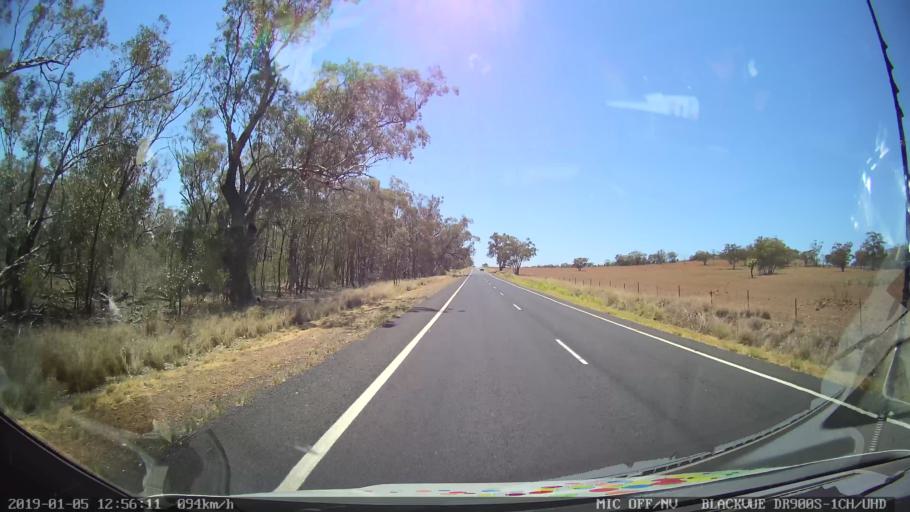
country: AU
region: New South Wales
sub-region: Warrumbungle Shire
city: Coonabarabran
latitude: -31.1162
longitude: 149.7168
